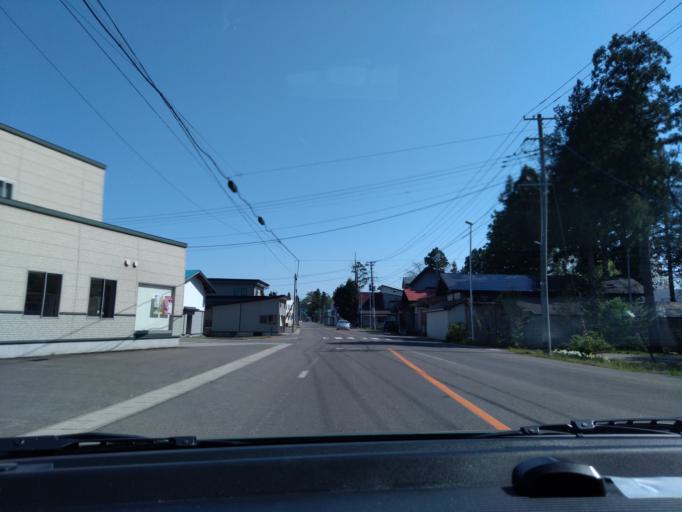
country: JP
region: Akita
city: Kakunodatemachi
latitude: 39.5320
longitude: 140.5854
